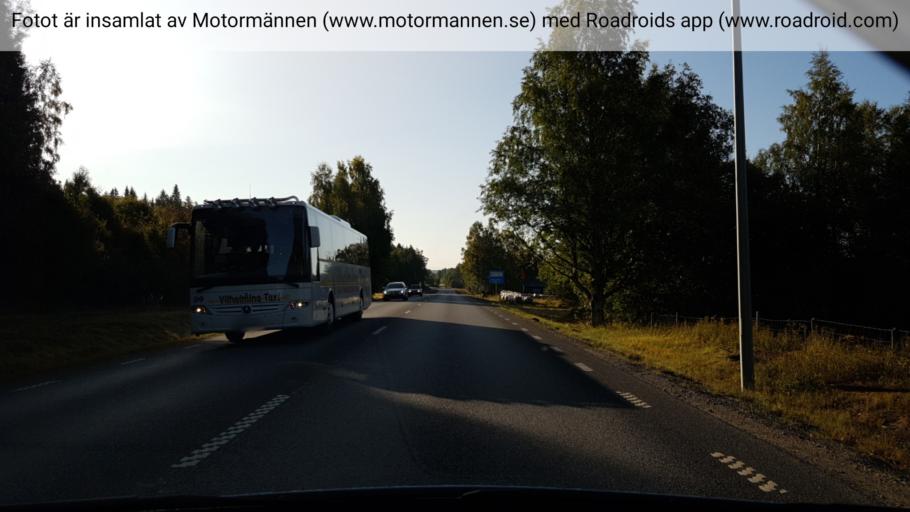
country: SE
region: Vaesterbotten
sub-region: Umea Kommun
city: Roback
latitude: 63.8597
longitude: 20.0908
